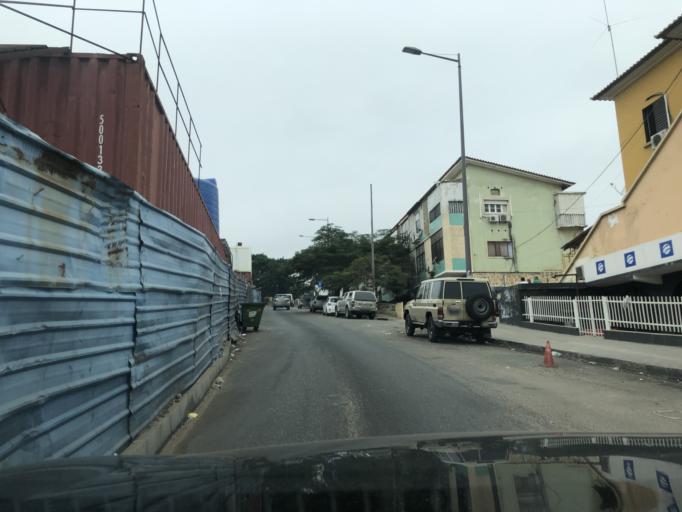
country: AO
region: Luanda
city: Luanda
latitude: -8.8211
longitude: 13.2327
